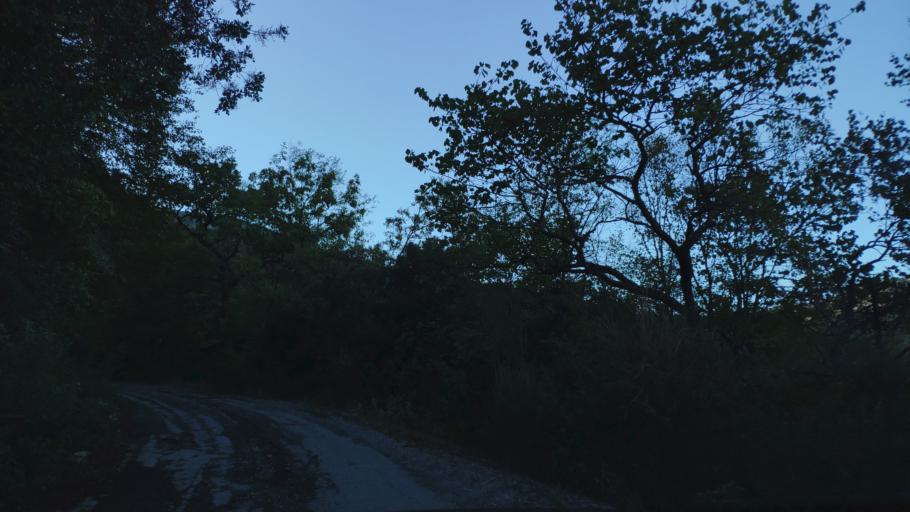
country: GR
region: Peloponnese
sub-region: Nomos Arkadias
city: Dimitsana
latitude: 37.5577
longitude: 22.0448
